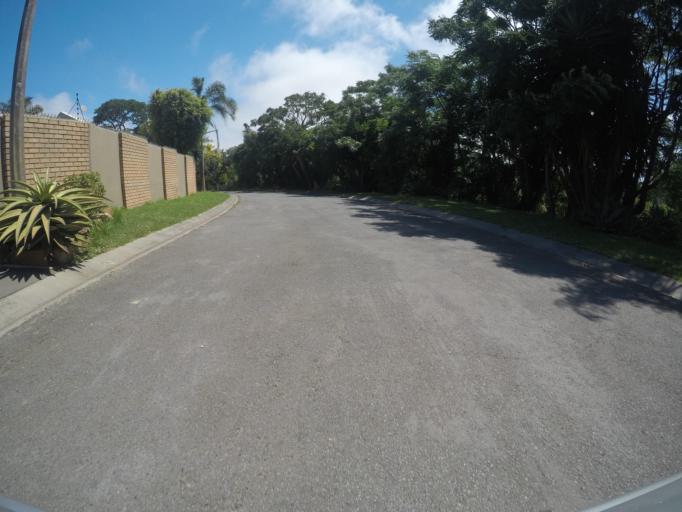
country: ZA
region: Eastern Cape
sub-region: Buffalo City Metropolitan Municipality
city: East London
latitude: -32.9728
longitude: 27.9054
